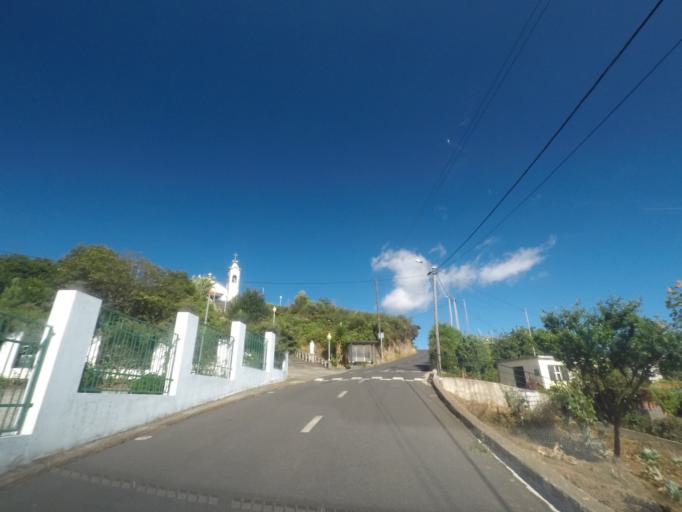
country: PT
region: Madeira
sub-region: Ribeira Brava
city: Campanario
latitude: 32.6947
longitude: -17.0285
